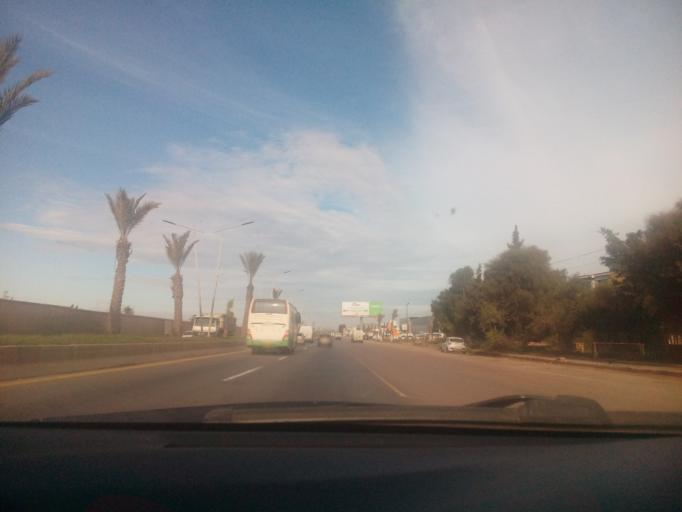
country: DZ
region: Oran
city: Es Senia
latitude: 35.6170
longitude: -0.5841
